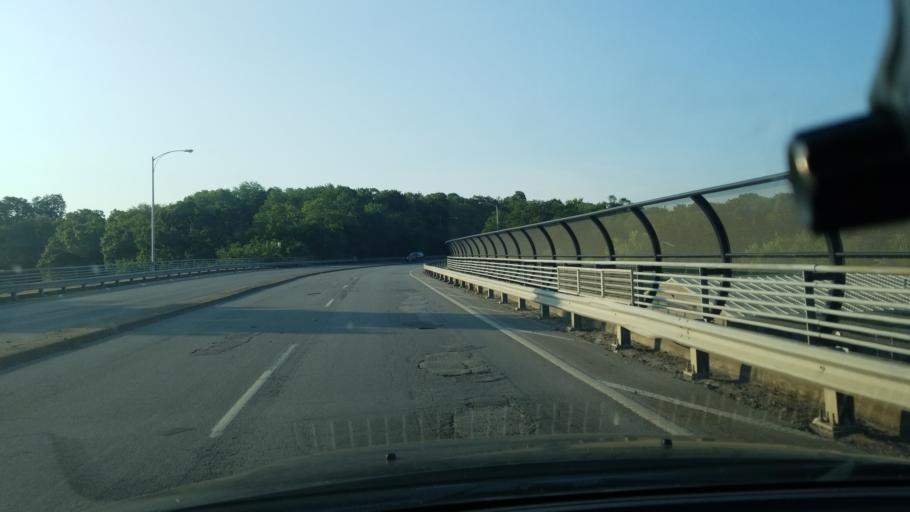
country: US
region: Texas
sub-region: Dallas County
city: Dallas
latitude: 32.7403
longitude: -96.8138
